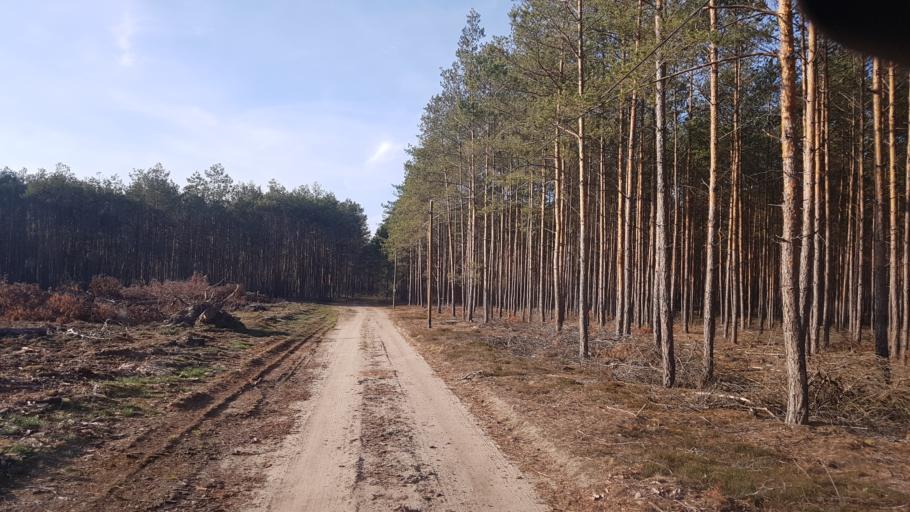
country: DE
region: Brandenburg
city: Schilda
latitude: 51.6412
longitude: 13.3536
